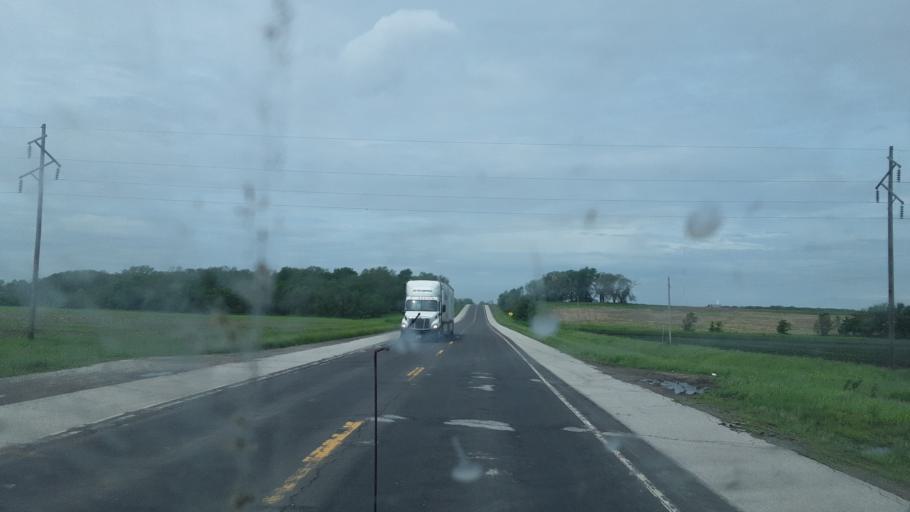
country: US
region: Illinois
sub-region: Hancock County
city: Warsaw
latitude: 40.3943
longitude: -91.5589
